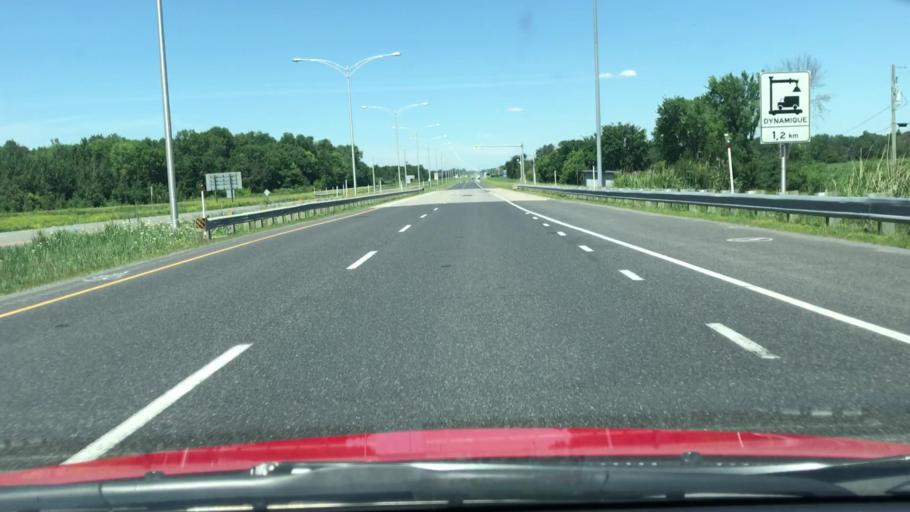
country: US
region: New York
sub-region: Clinton County
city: Champlain
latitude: 45.0217
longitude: -73.4529
